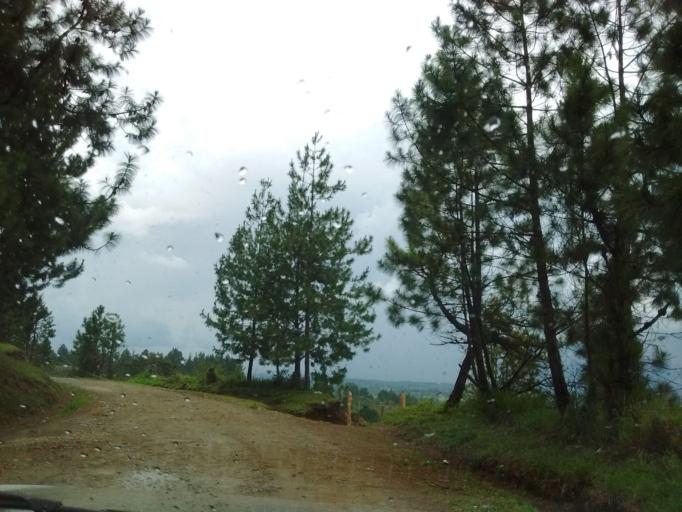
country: CO
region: Cauca
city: Cajibio
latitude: 2.5689
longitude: -76.6426
